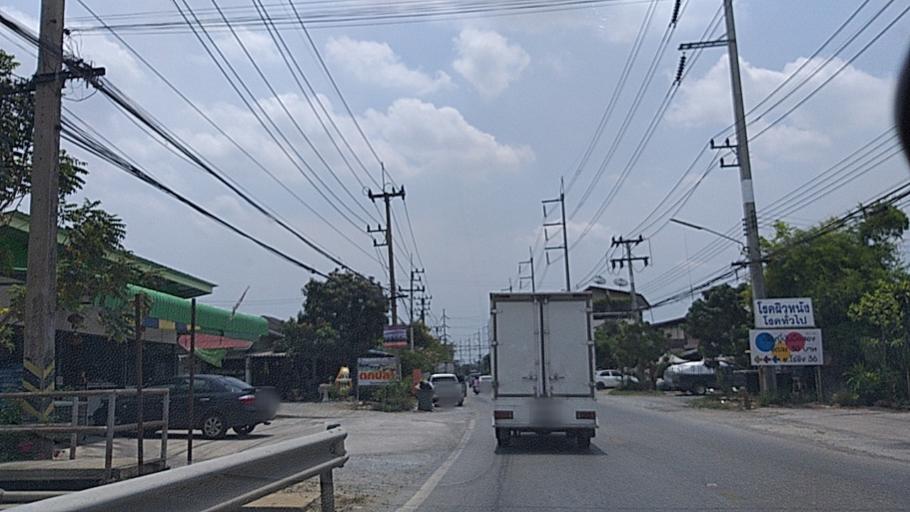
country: TH
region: Nakhon Pathom
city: Salaya
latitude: 13.7595
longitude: 100.2837
